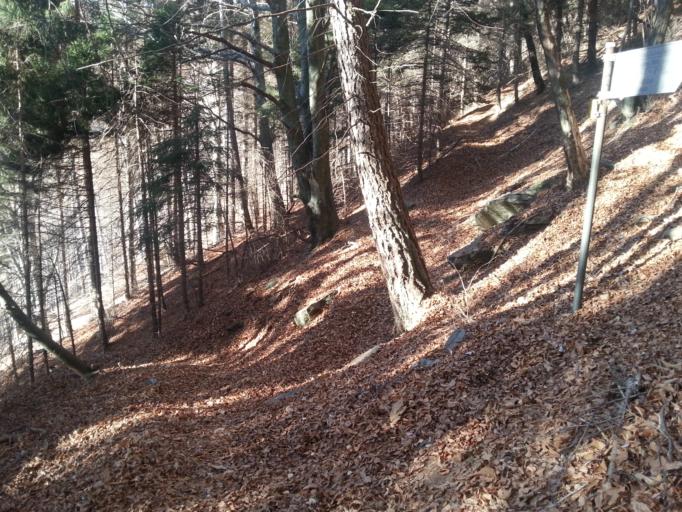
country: IT
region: Lombardy
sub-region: Provincia di Varese
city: Curiglia
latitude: 46.0411
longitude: 8.8557
